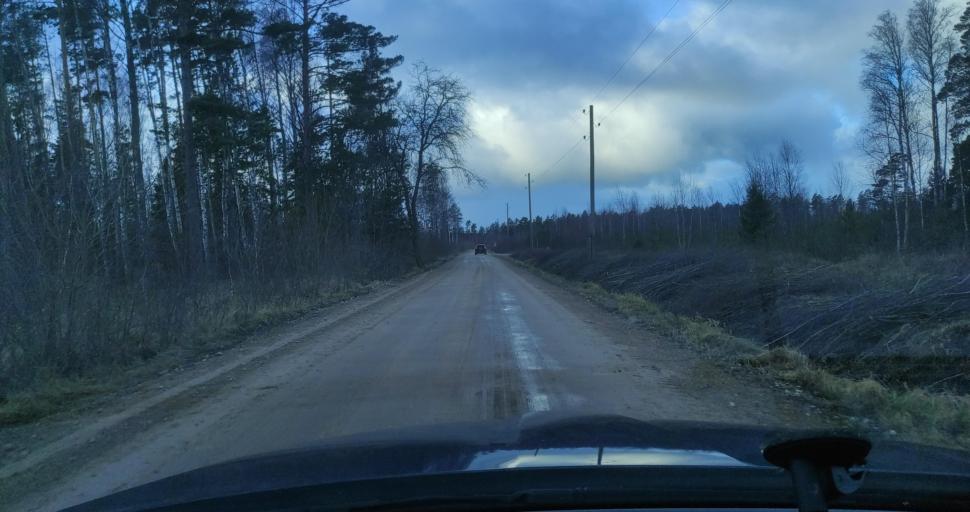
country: LV
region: Pavilostas
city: Pavilosta
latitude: 56.8581
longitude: 21.1692
